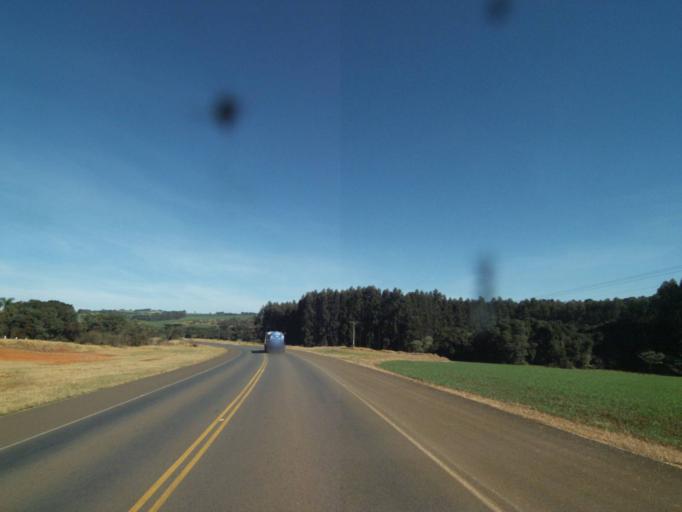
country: BR
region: Parana
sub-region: Tibagi
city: Tibagi
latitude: -24.4731
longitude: -50.4455
